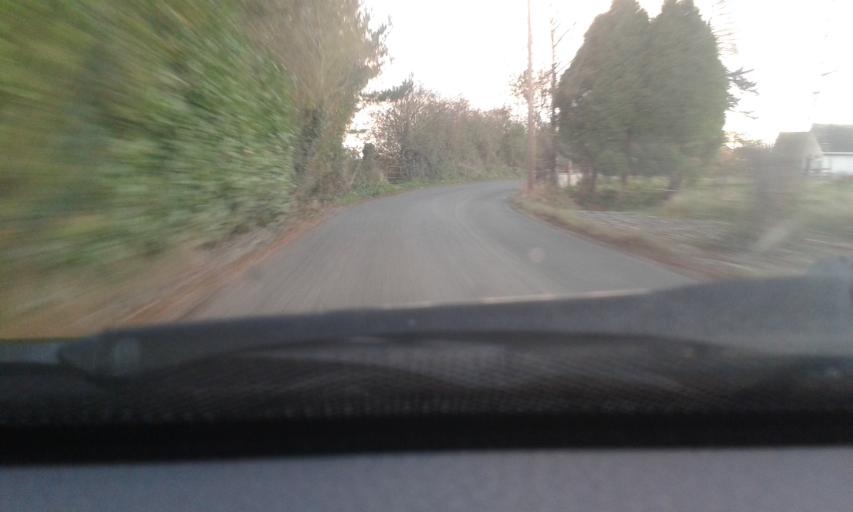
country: IE
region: Leinster
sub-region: Kildare
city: Monasterevin
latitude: 53.1434
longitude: -7.0364
